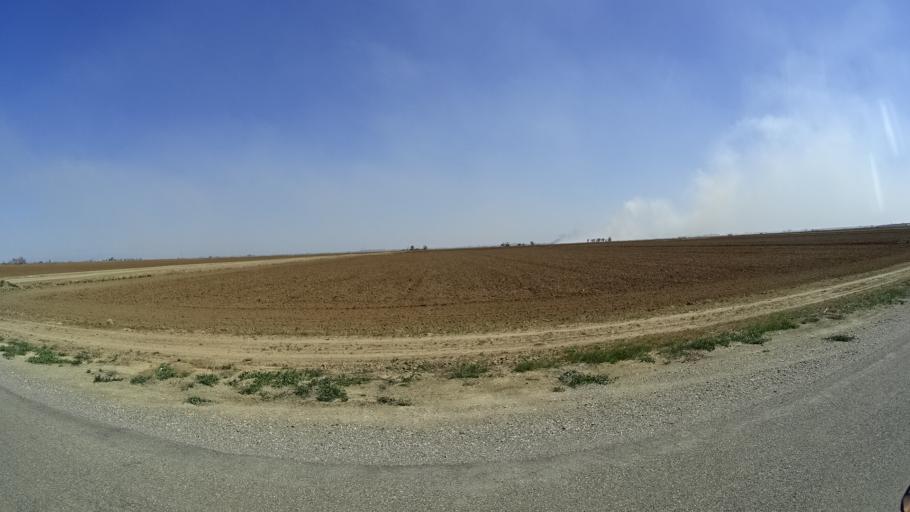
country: US
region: California
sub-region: Colusa County
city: Maxwell
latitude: 39.3876
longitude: -122.2483
